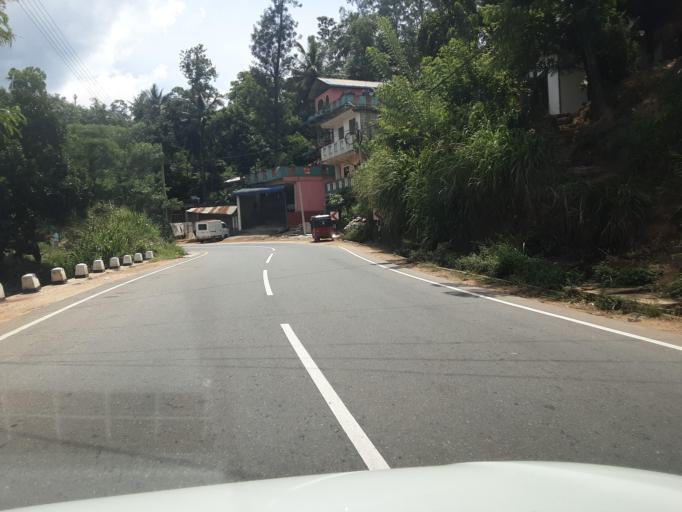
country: LK
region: Central
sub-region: Nuwara Eliya District
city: Nuwara Eliya
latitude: 6.9237
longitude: 80.8993
